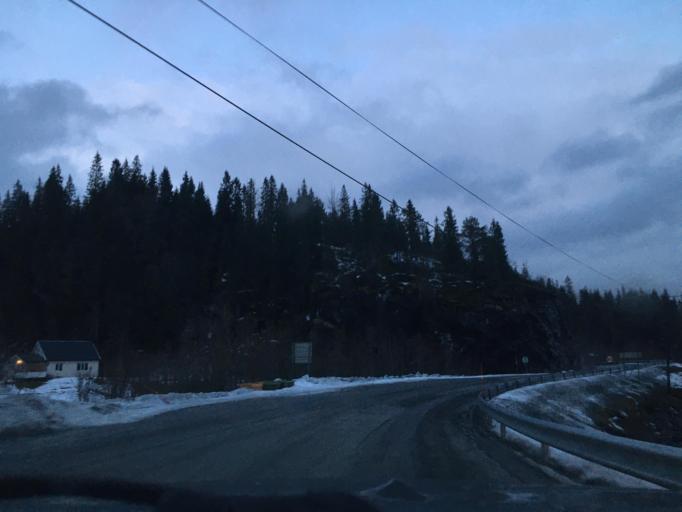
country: NO
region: Nordland
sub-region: Rana
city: Hauknes
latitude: 66.3047
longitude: 13.9437
